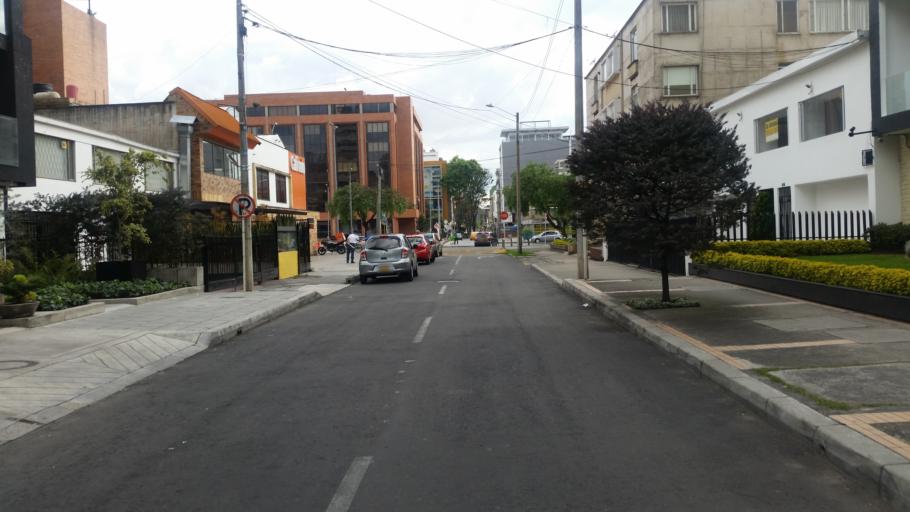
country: CO
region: Bogota D.C.
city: Barrio San Luis
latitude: 4.6713
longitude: -74.0561
